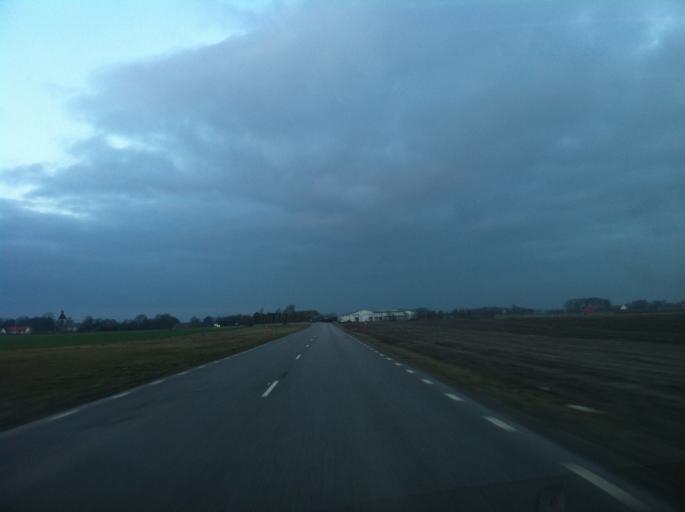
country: SE
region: Skane
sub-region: Svalovs Kommun
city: Teckomatorp
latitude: 55.8312
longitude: 13.0944
